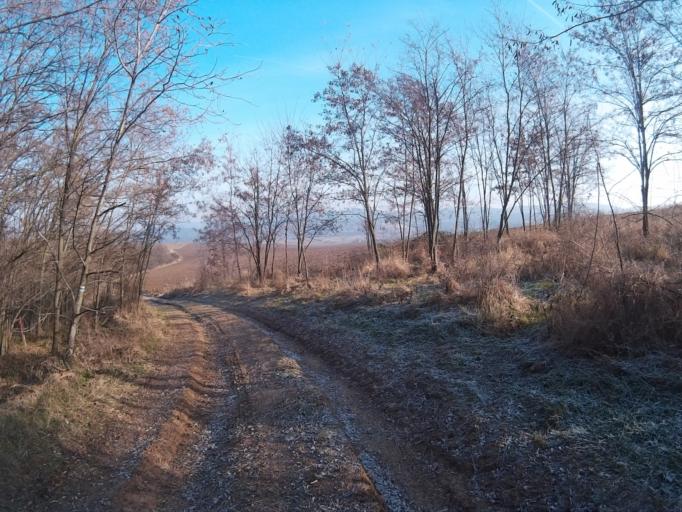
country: HU
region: Nograd
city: Bercel
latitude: 47.9294
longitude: 19.4235
